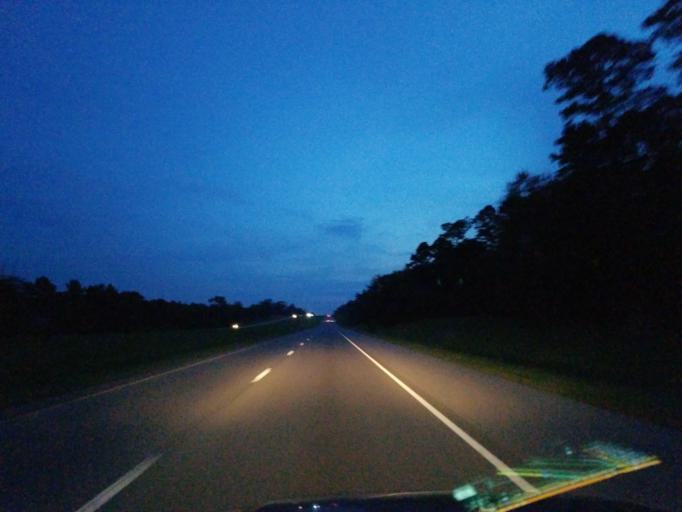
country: US
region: Mississippi
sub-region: Jones County
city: Ellisville
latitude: 31.5691
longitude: -89.2511
